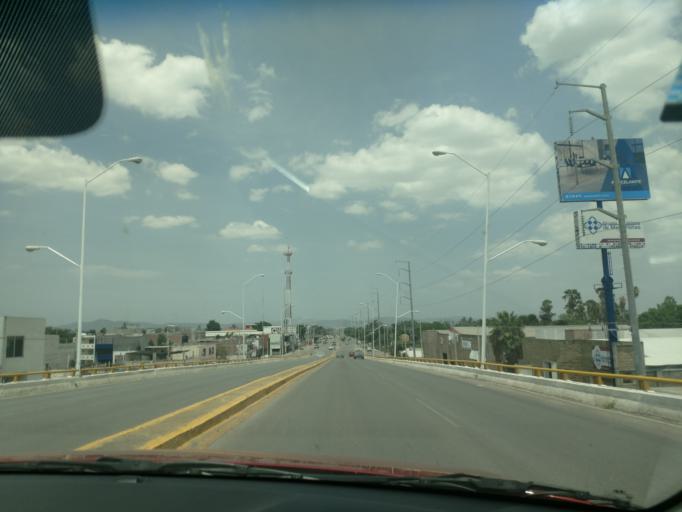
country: MX
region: San Luis Potosi
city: Rio Verde
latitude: 21.9232
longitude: -99.9928
